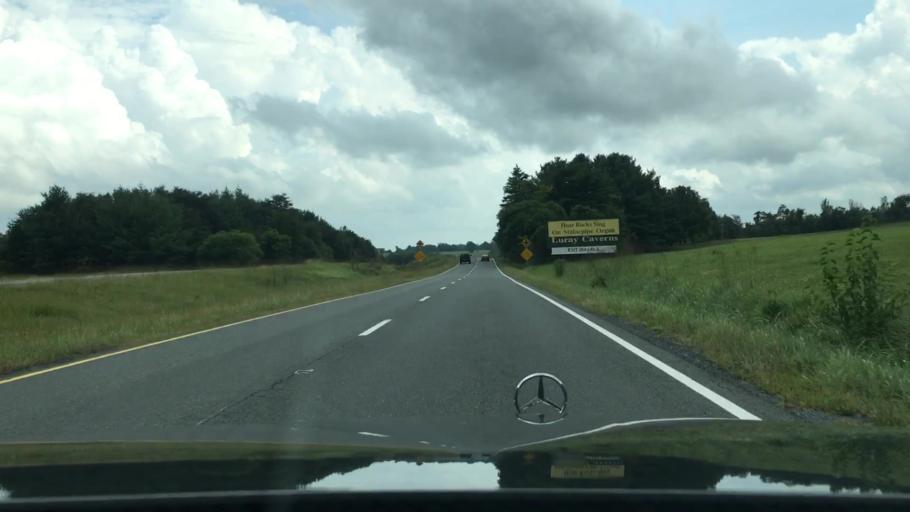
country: US
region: Virginia
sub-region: Frederick County
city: Shawnee Land
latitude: 39.3867
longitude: -78.3013
